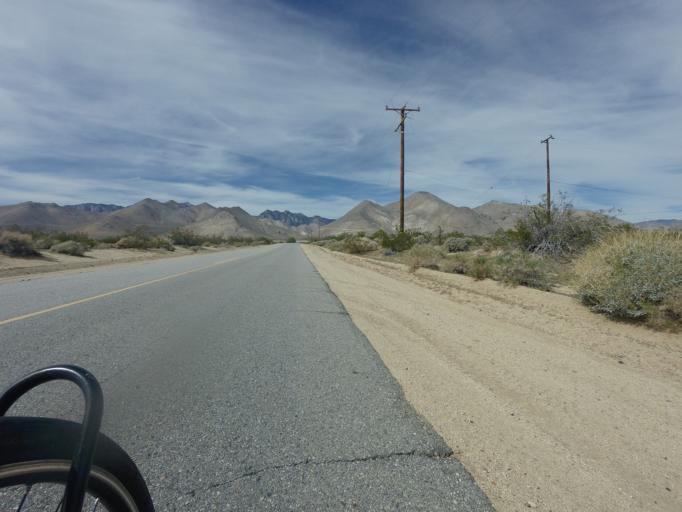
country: US
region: California
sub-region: Kern County
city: Inyokern
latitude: 35.7764
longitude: -117.8685
